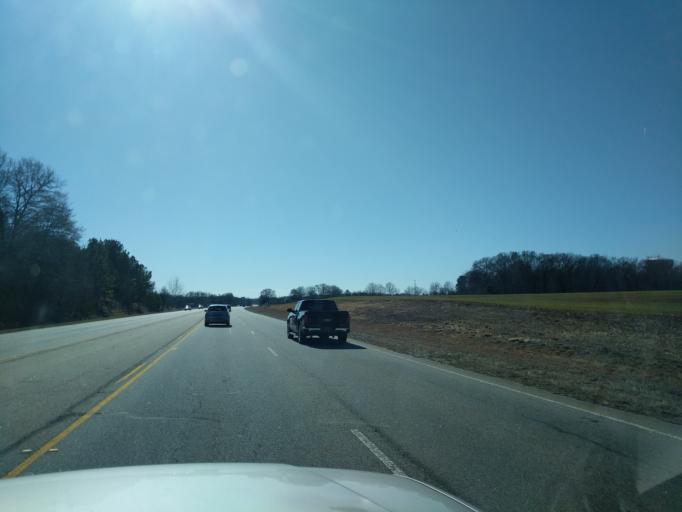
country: US
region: South Carolina
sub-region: Anderson County
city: Northlake
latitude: 34.6254
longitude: -82.6040
